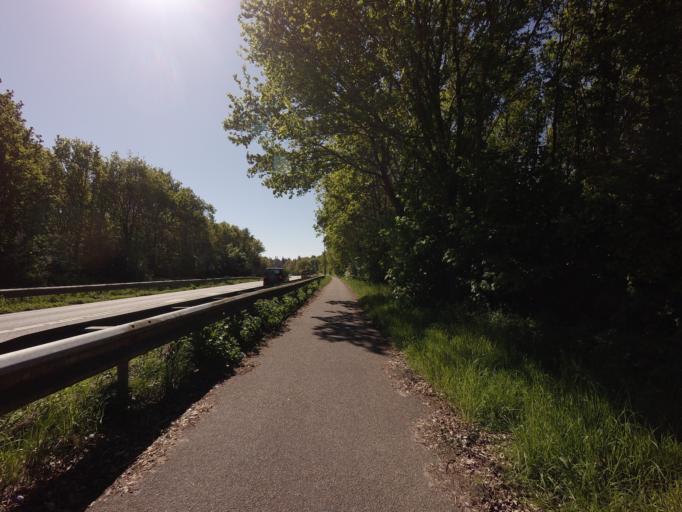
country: NL
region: North Brabant
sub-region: Gemeente Rucphen
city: Rucphen
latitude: 51.5510
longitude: 4.5450
